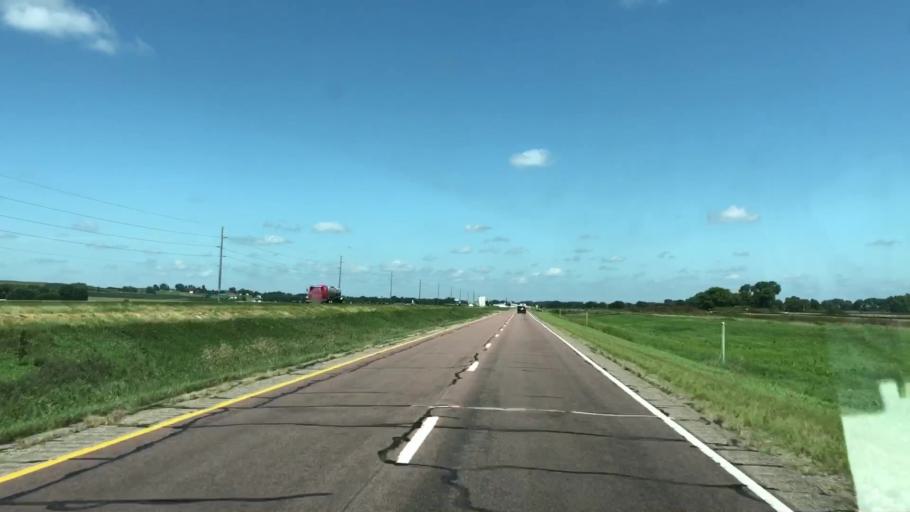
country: US
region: Iowa
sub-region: Plymouth County
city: Le Mars
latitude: 42.6975
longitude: -96.2592
